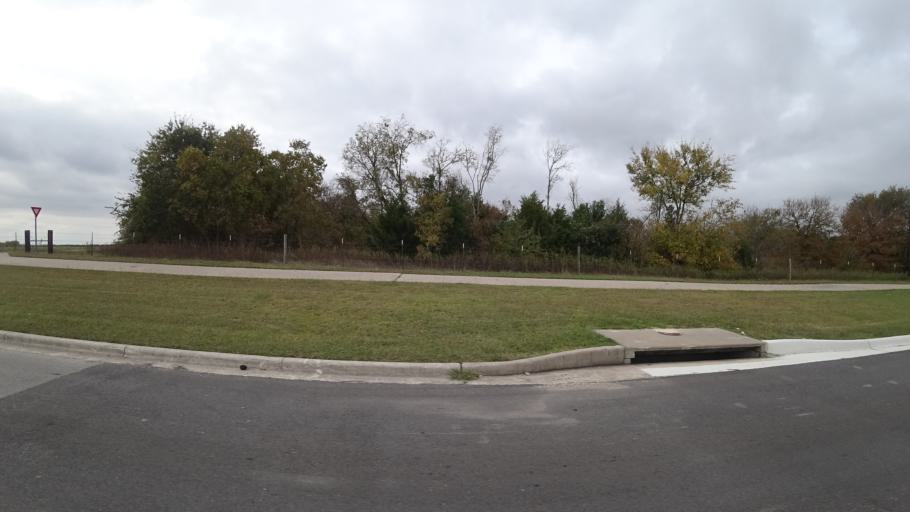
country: US
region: Texas
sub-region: Travis County
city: Pflugerville
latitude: 30.4280
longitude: -97.5975
